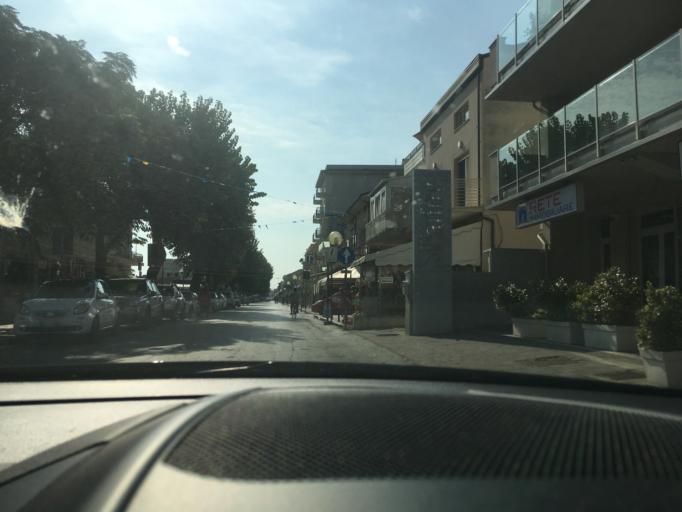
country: IT
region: Emilia-Romagna
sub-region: Provincia di Rimini
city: Santa Giustina
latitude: 44.1078
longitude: 12.5117
